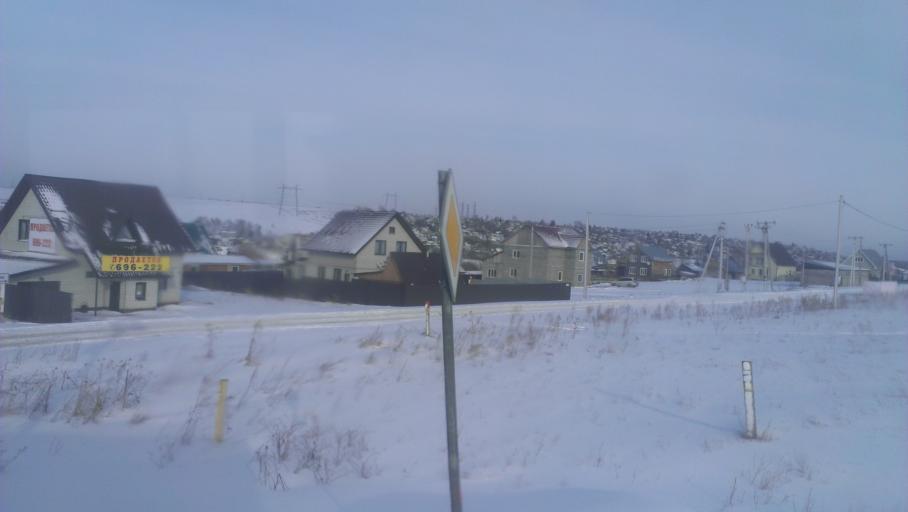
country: RU
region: Altai Krai
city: Gon'ba
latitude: 53.4135
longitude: 83.5536
